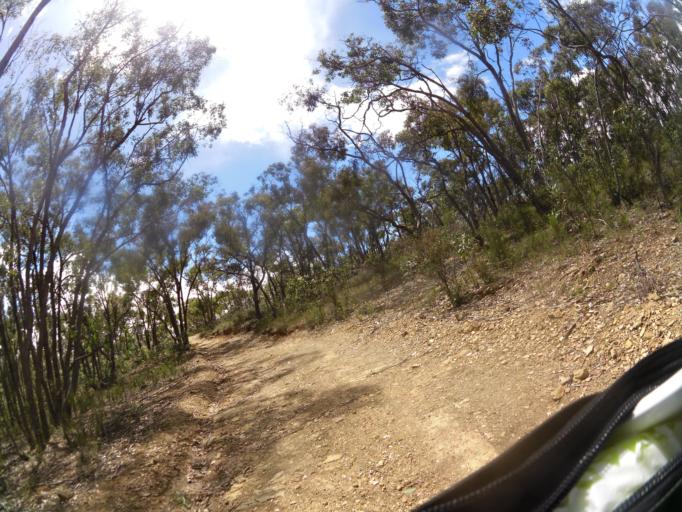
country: AU
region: Victoria
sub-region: Mount Alexander
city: Castlemaine
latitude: -37.0707
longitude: 144.2633
